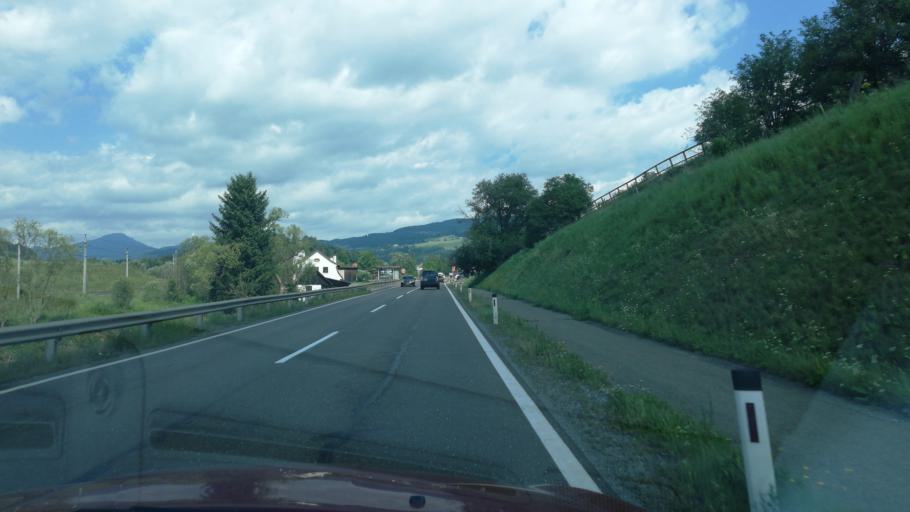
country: AT
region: Styria
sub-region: Politischer Bezirk Murau
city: Sankt Marein bei Neumarkt
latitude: 47.0589
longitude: 14.4326
